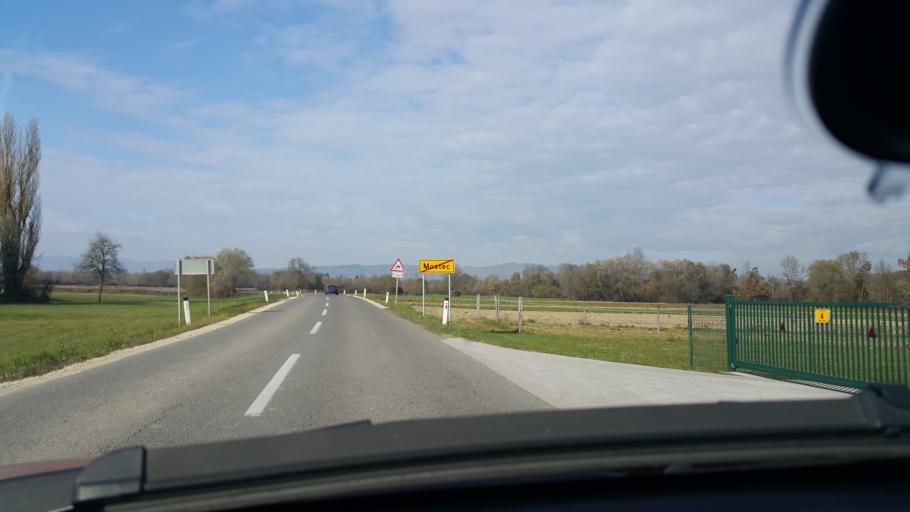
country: SI
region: Brezice
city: Brezice
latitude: 45.9001
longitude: 15.6263
